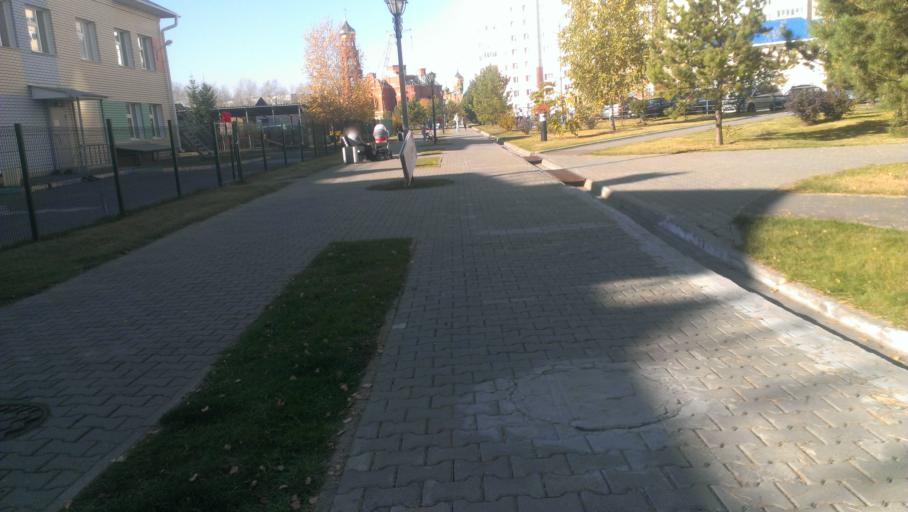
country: RU
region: Altai Krai
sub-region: Gorod Barnaulskiy
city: Barnaul
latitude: 53.3574
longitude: 83.6926
